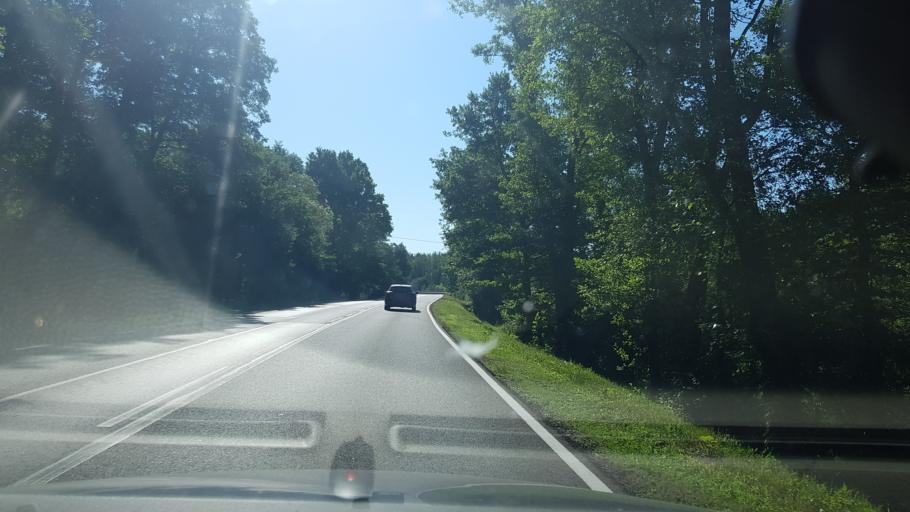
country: PL
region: Masovian Voivodeship
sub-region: Powiat wyszkowski
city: Branszczyk
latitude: 52.5559
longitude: 21.5933
